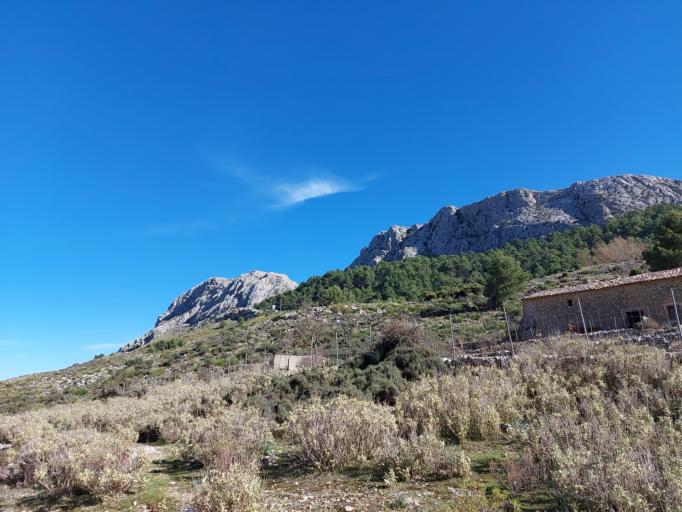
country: ES
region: Balearic Islands
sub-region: Illes Balears
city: Fornalutx
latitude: 39.7698
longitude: 2.7682
